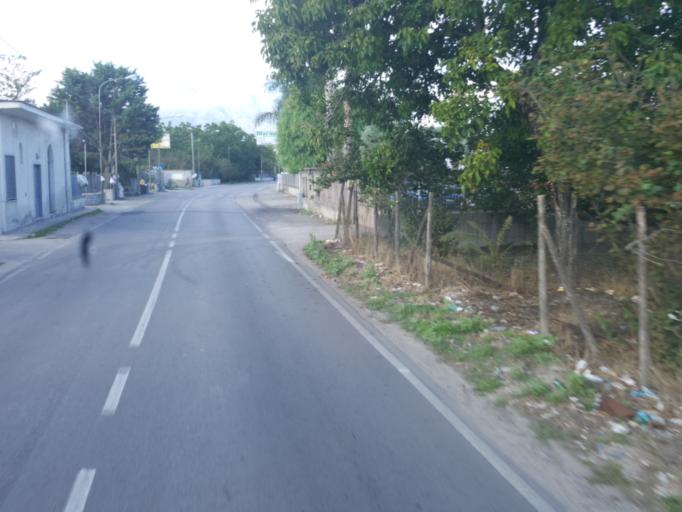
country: IT
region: Campania
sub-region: Provincia di Napoli
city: Piazzolla
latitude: 40.8889
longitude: 14.5172
